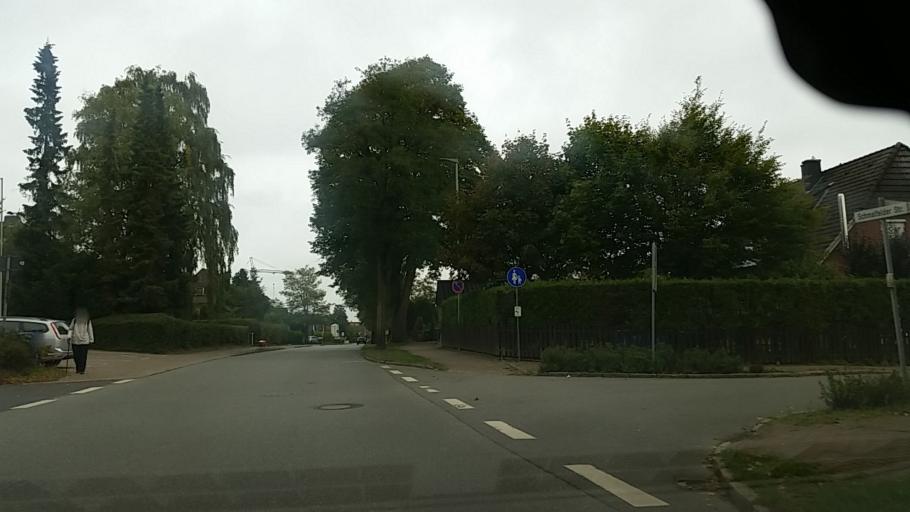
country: DE
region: Schleswig-Holstein
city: Kaltenkirchen
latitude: 53.8402
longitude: 9.9591
